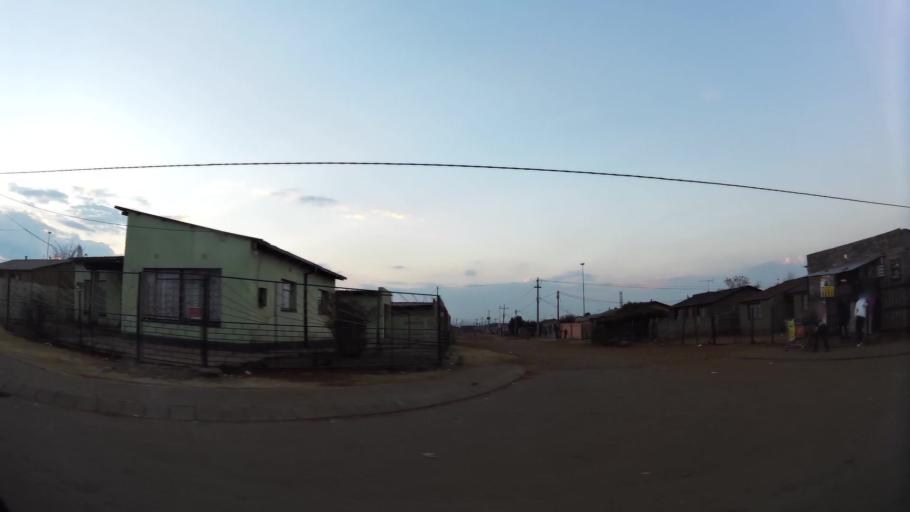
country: ZA
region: Gauteng
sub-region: City of Johannesburg Metropolitan Municipality
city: Orange Farm
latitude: -26.5571
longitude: 27.8693
